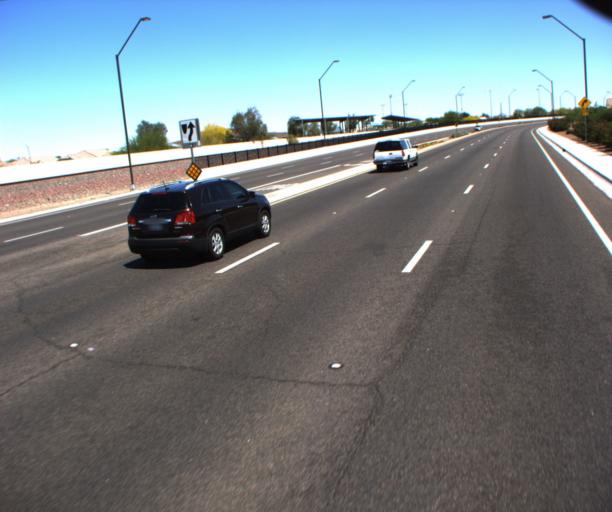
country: US
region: Arizona
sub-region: Maricopa County
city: Peoria
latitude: 33.5913
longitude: -112.2511
